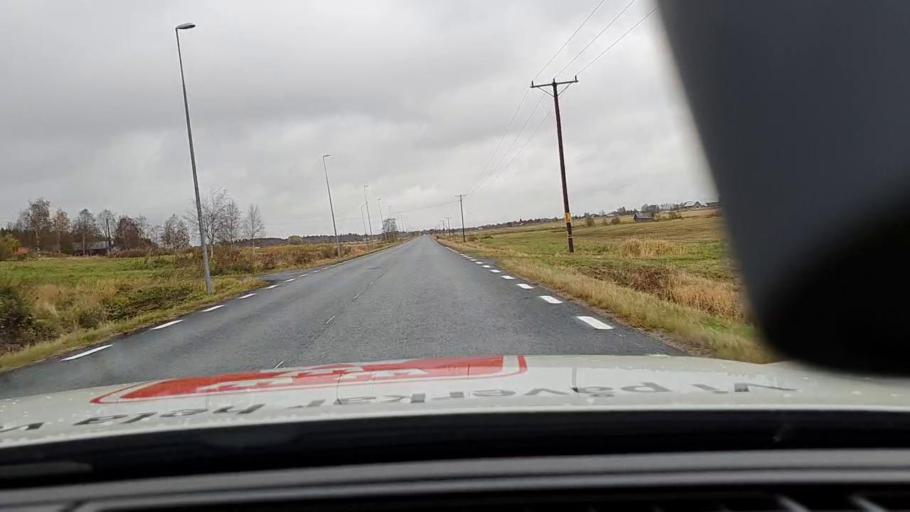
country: FI
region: Lapland
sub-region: Kemi-Tornio
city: Tornio
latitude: 65.9781
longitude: 24.0282
